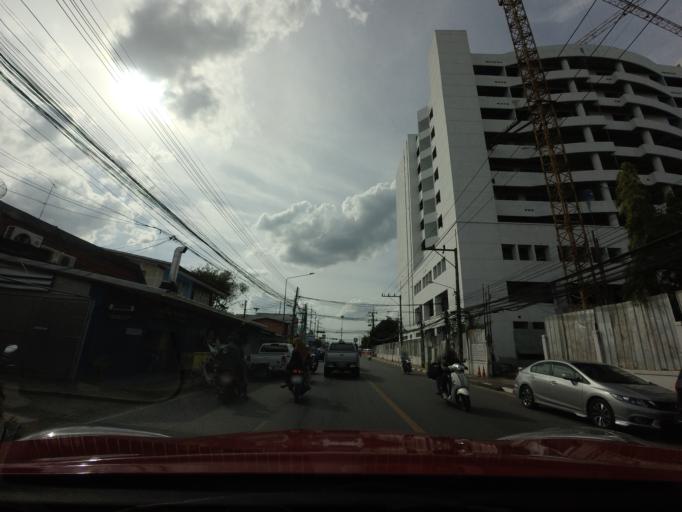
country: TH
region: Yala
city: Yala
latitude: 6.5469
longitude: 101.2761
